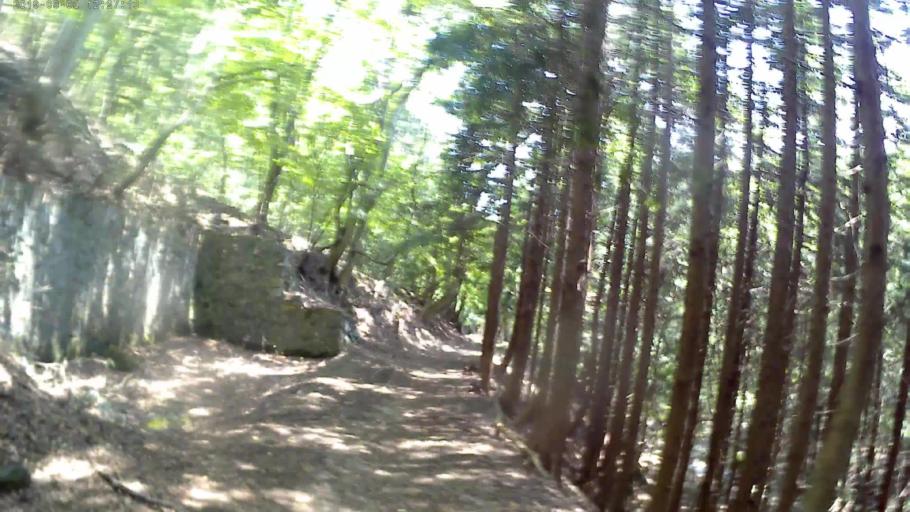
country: JP
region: Yamanashi
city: Enzan
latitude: 35.6099
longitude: 138.7889
